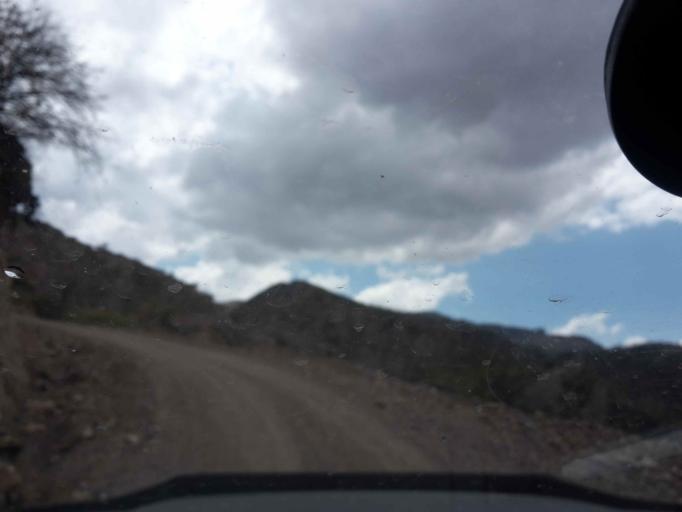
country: BO
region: Cochabamba
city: Sipe Sipe
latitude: -17.5241
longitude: -66.5552
